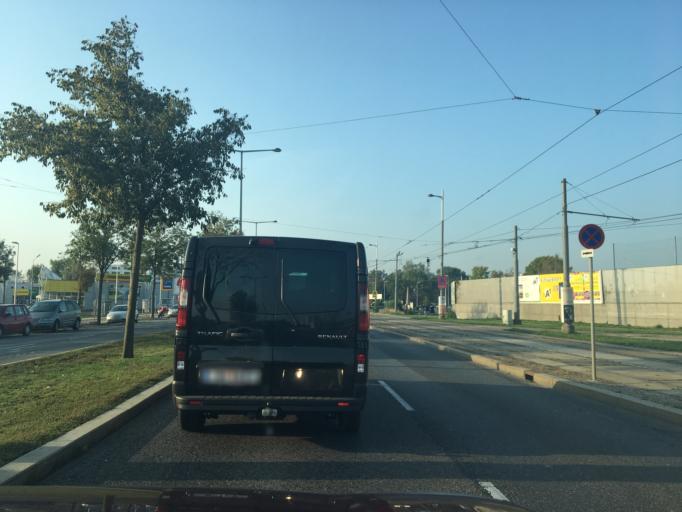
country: AT
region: Lower Austria
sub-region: Politischer Bezirk Korneuburg
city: Hagenbrunn
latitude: 48.2832
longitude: 16.4126
